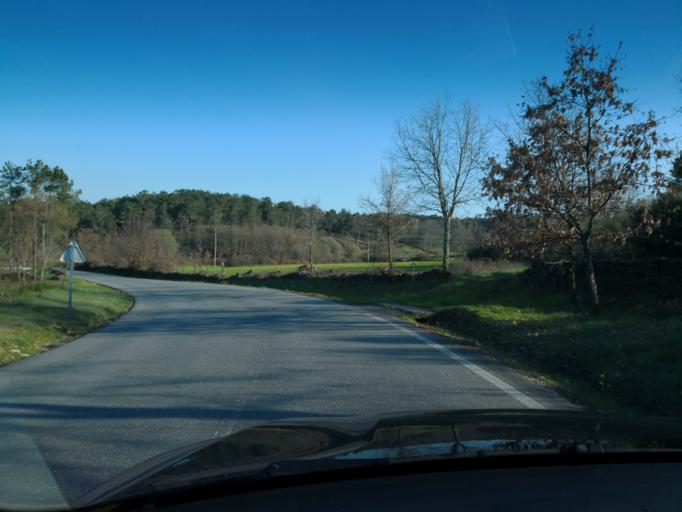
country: PT
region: Vila Real
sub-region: Sabrosa
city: Sabrosa
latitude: 41.3538
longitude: -7.6128
